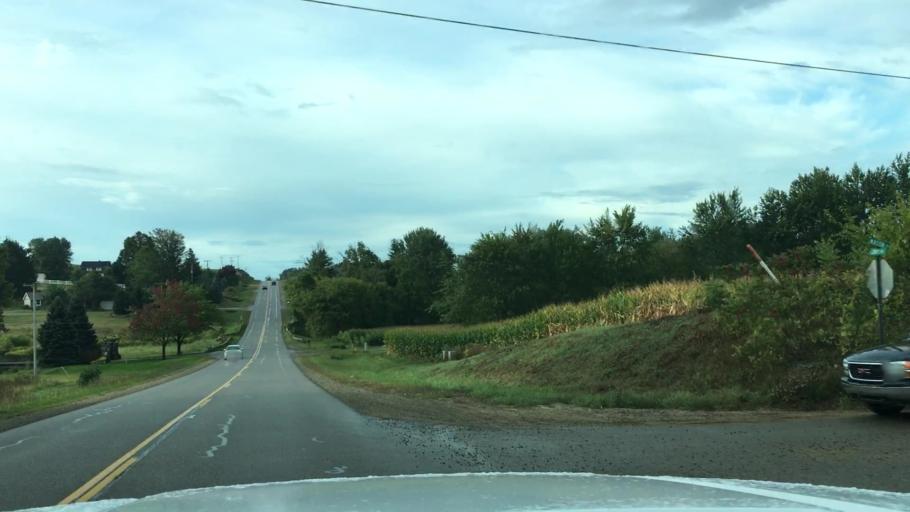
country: US
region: Michigan
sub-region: Ottawa County
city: Hudsonville
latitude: 42.7748
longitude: -85.8417
